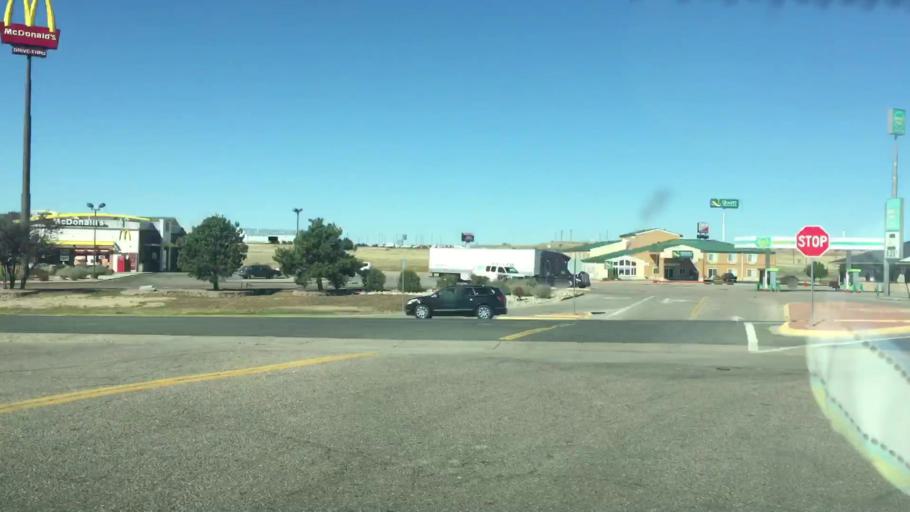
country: US
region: Colorado
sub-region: Lincoln County
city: Limon
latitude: 39.2706
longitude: -103.7074
